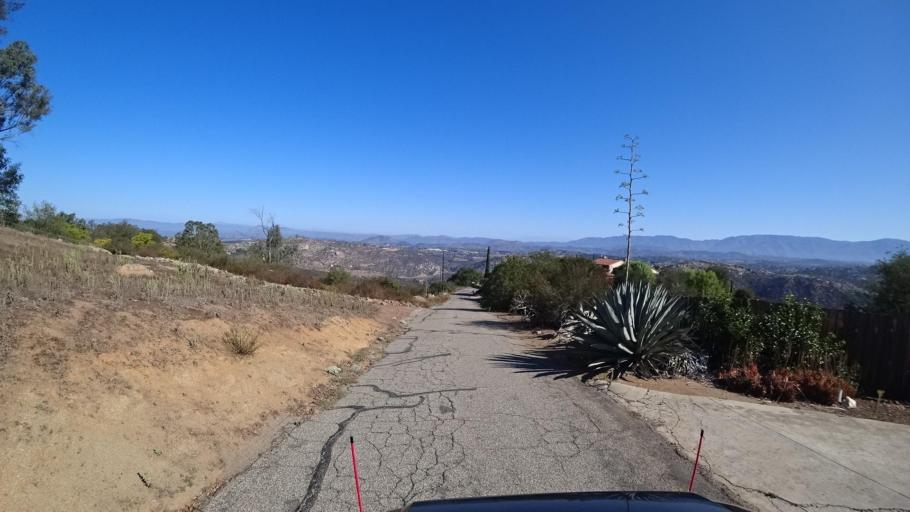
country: US
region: California
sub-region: San Diego County
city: Hidden Meadows
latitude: 33.2321
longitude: -117.1104
